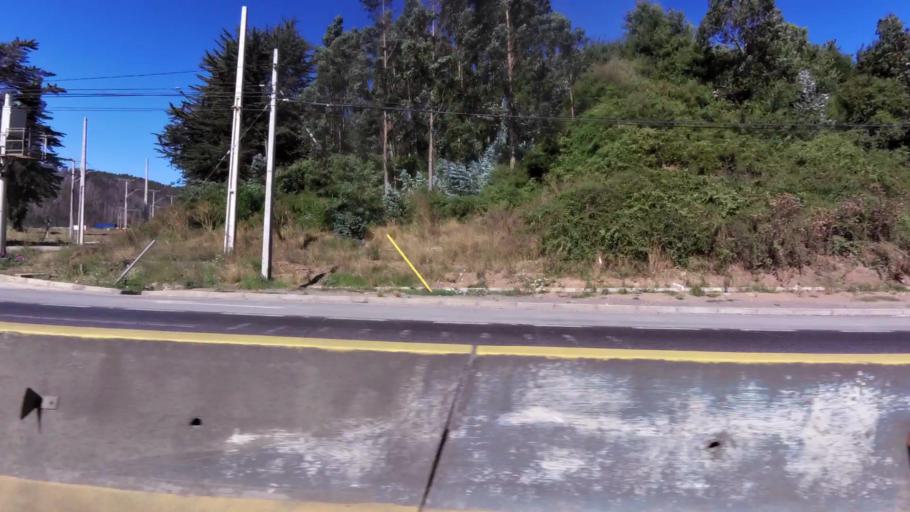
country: CL
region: Biobio
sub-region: Provincia de Concepcion
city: Concepcion
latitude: -36.7996
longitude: -73.0258
